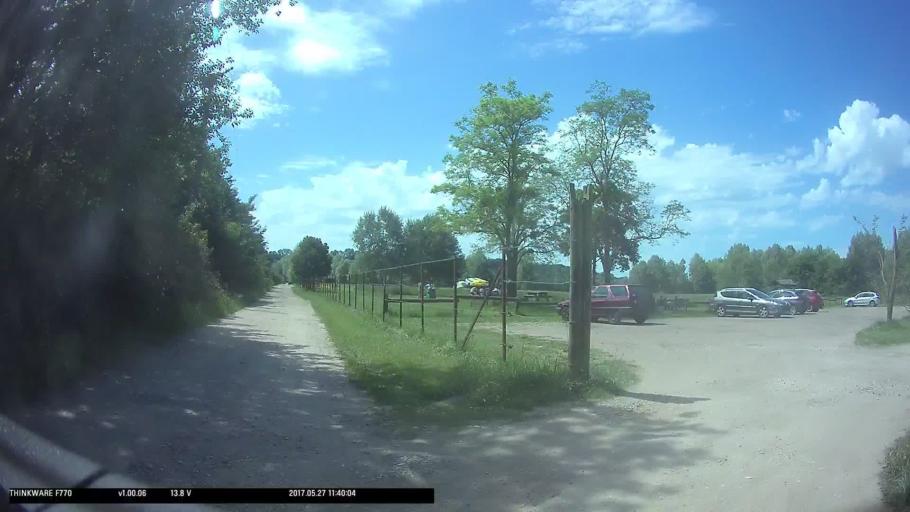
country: FR
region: Haute-Normandie
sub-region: Departement de l'Eure
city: Neaufles-Saint-Martin
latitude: 49.2708
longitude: 1.7257
